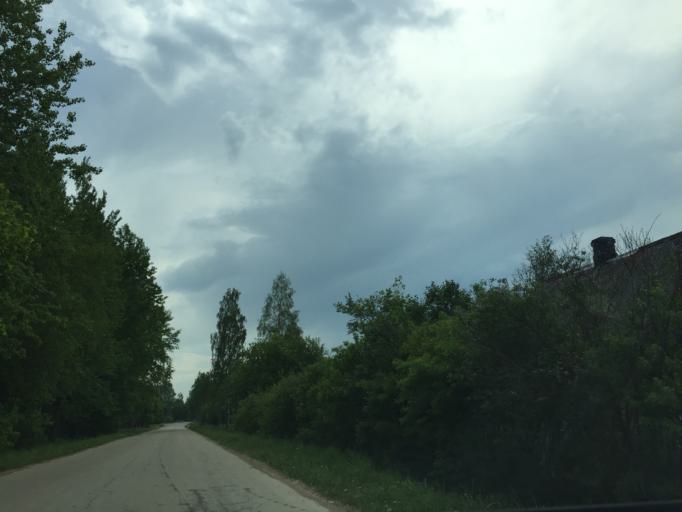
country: LV
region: Livani
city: Livani
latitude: 56.5410
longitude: 26.2443
